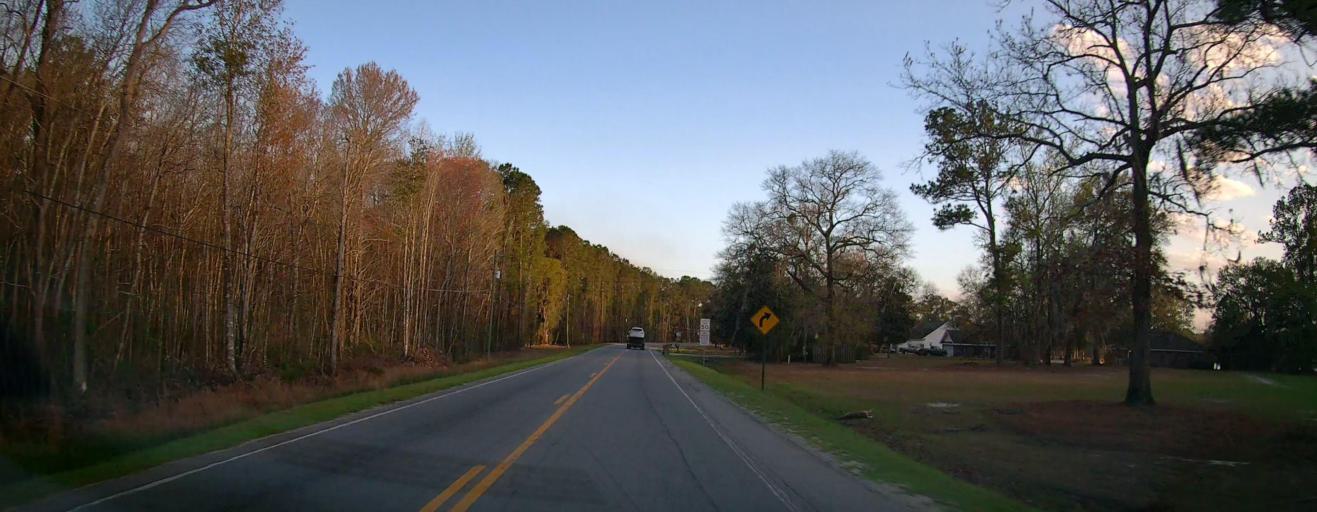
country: US
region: Georgia
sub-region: Chatham County
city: Bloomingdale
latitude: 32.1672
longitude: -81.3857
